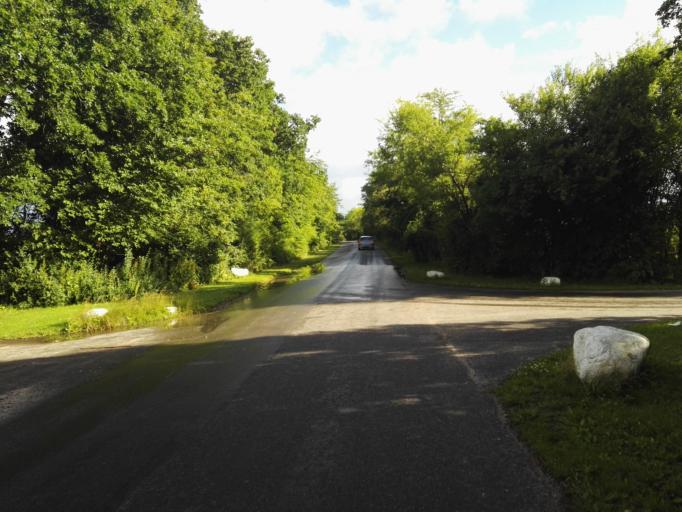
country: DK
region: Capital Region
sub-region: Ballerup Kommune
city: Ballerup
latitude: 55.7171
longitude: 12.3400
